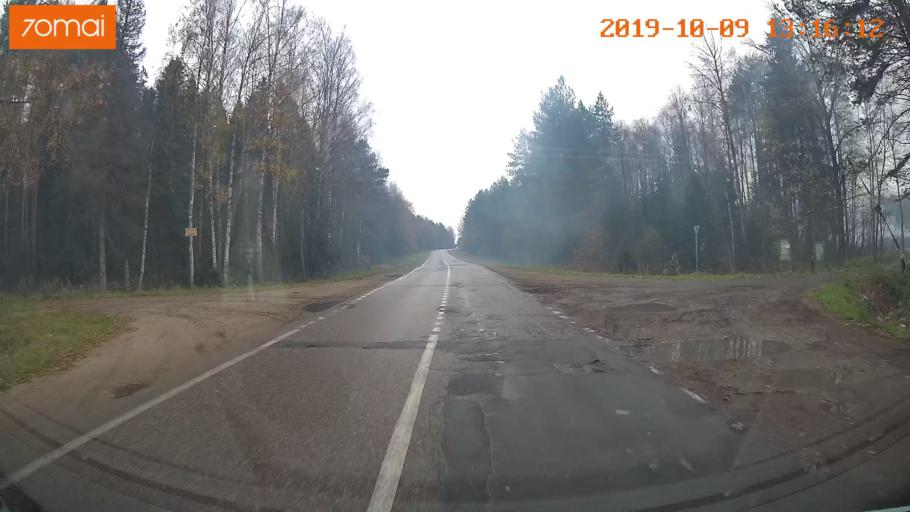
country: RU
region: Jaroslavl
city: Lyubim
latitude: 58.3629
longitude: 40.7625
